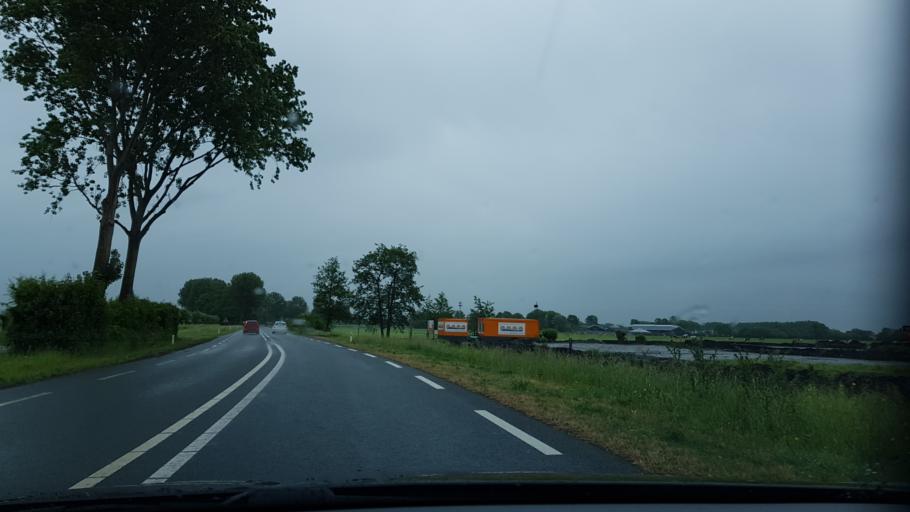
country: NL
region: South Holland
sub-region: Gemeente Leiderdorp
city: Leiderdorp
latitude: 52.1667
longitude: 4.5945
